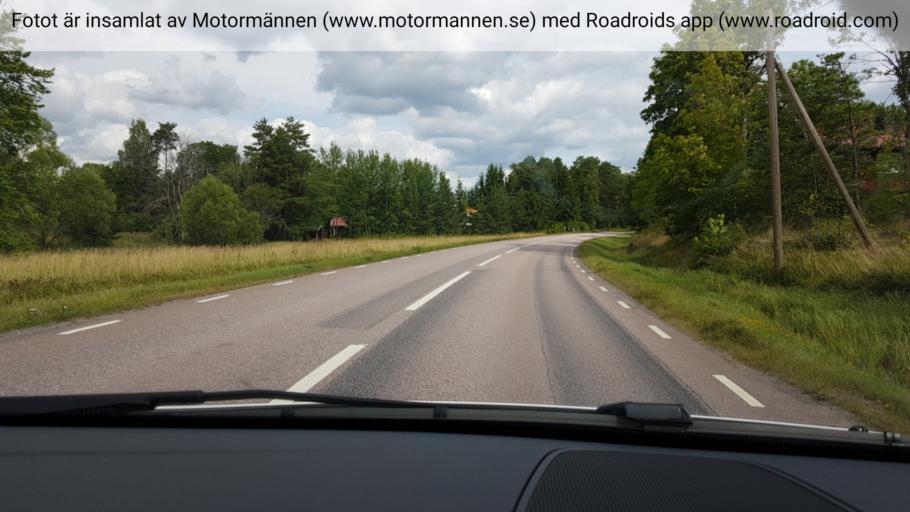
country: SE
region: Stockholm
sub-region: Norrtalje Kommun
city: Nykvarn
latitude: 59.8601
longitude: 18.0620
